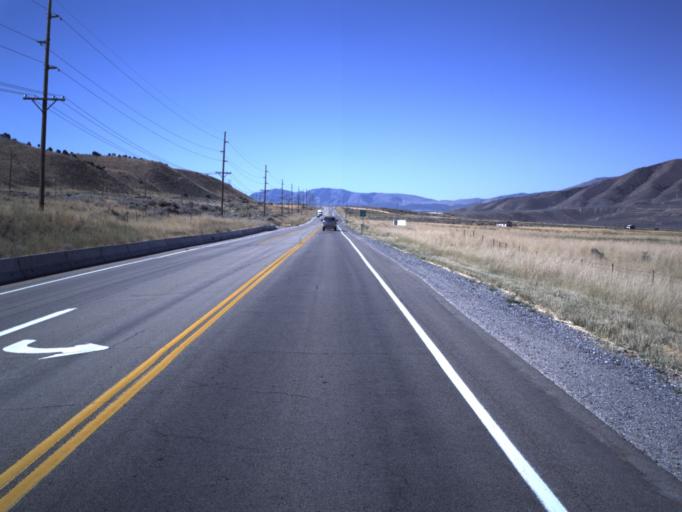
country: US
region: Utah
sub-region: Tooele County
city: Tooele
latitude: 40.4887
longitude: -112.3361
